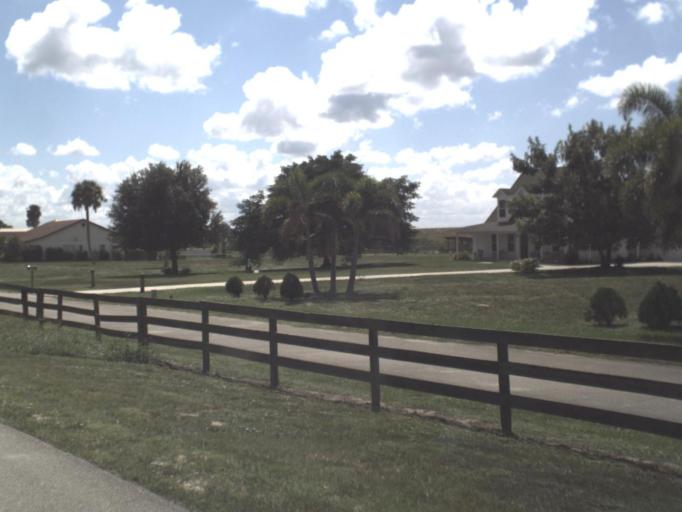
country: US
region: Florida
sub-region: Okeechobee County
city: Taylor Creek
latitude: 27.1421
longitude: -80.6919
